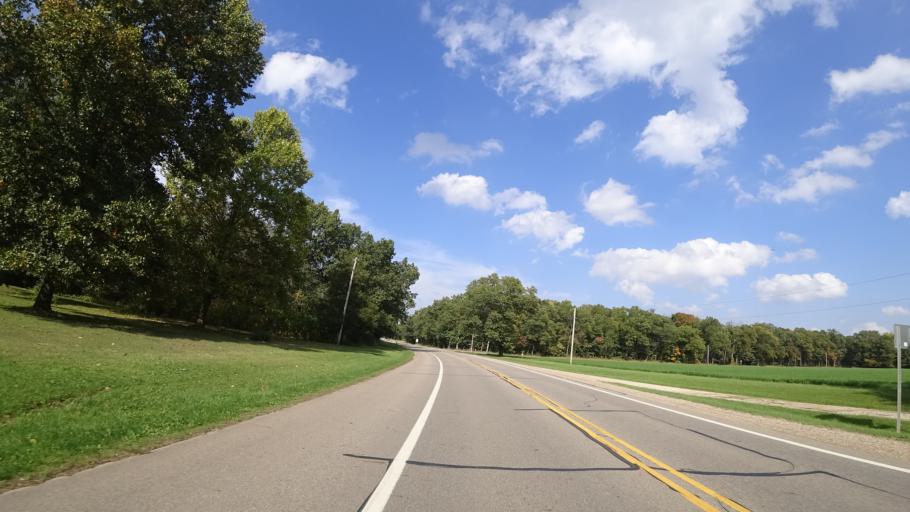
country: US
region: Michigan
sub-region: Saint Joseph County
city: Centreville
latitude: 41.9684
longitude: -85.5671
